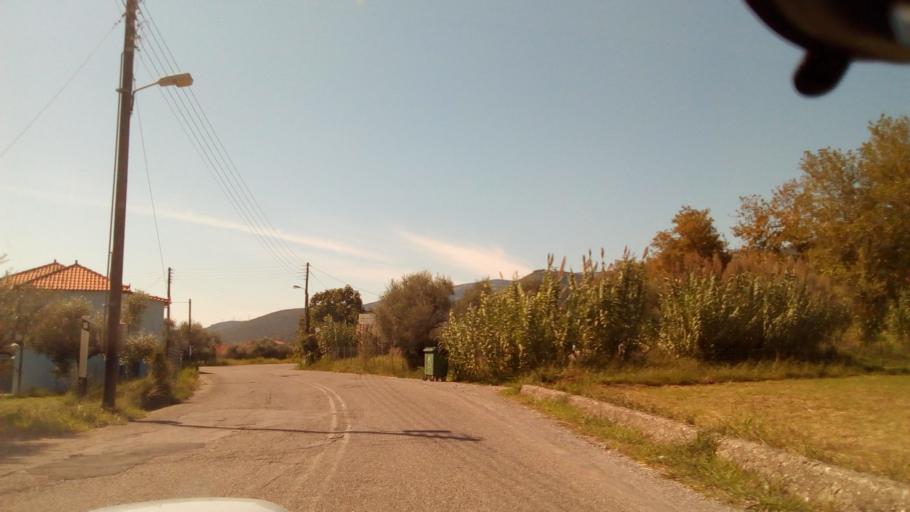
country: GR
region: West Greece
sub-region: Nomos Aitolias kai Akarnanias
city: Nafpaktos
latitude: 38.4176
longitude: 21.8903
